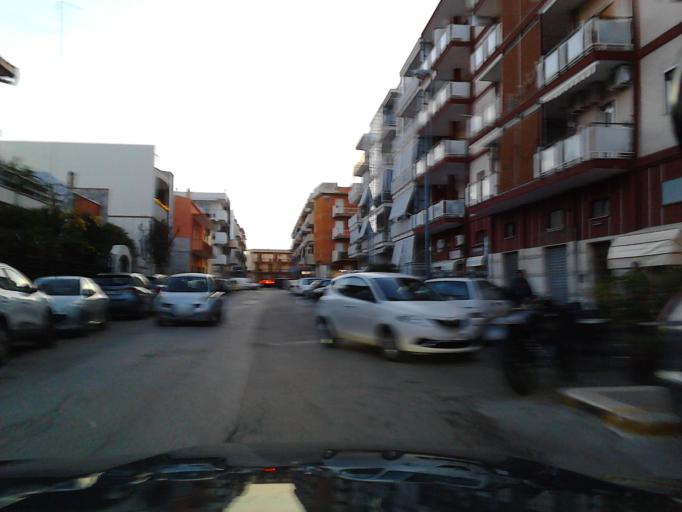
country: IT
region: Apulia
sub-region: Provincia di Bari
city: Valenzano
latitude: 41.0421
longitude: 16.8825
